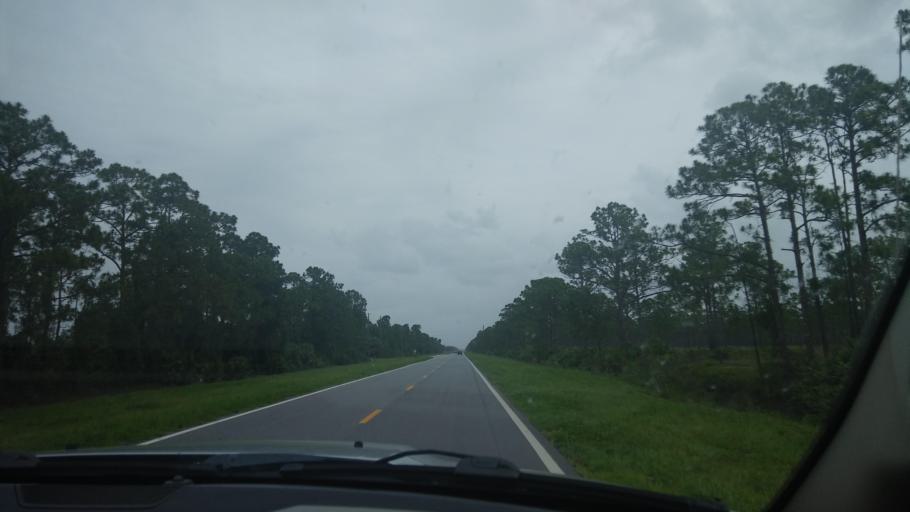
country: US
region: Florida
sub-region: Indian River County
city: Fellsmere
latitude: 27.8600
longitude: -80.6229
